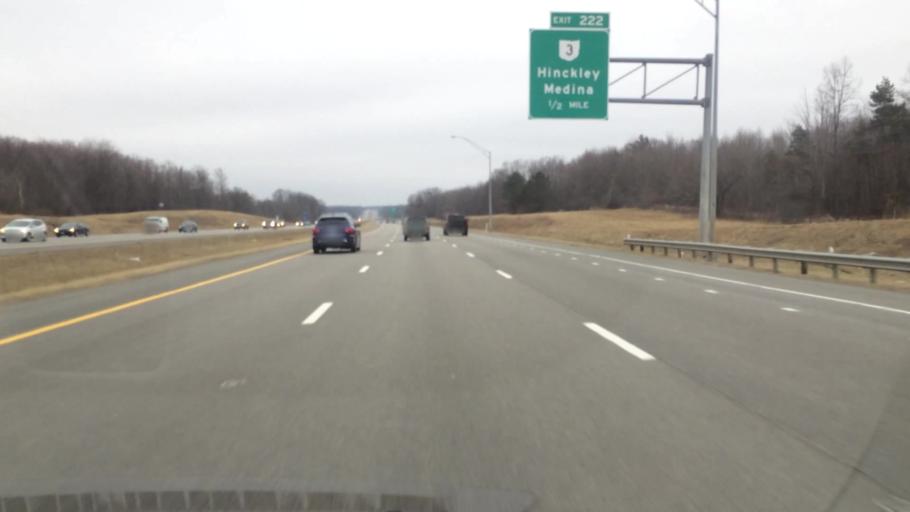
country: US
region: Ohio
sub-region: Medina County
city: Brunswick
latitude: 41.2044
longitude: -81.7932
